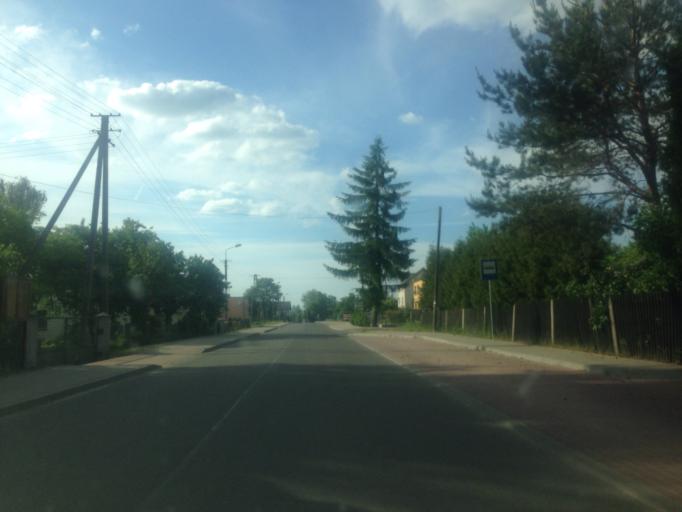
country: PL
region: Kujawsko-Pomorskie
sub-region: Powiat brodnicki
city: Brodnica
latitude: 53.3247
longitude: 19.4778
